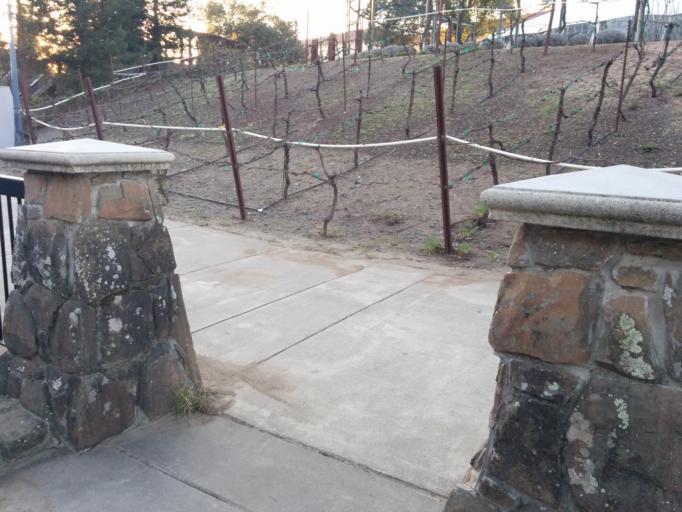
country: US
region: California
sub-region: Sonoma County
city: Santa Rosa
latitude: 38.4352
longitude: -122.7179
